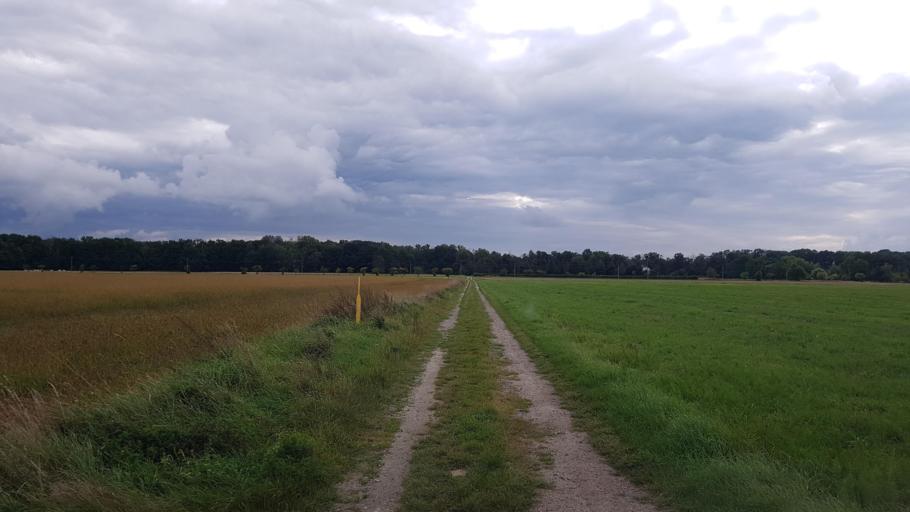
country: DE
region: Brandenburg
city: Doberlug-Kirchhain
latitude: 51.6369
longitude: 13.5740
